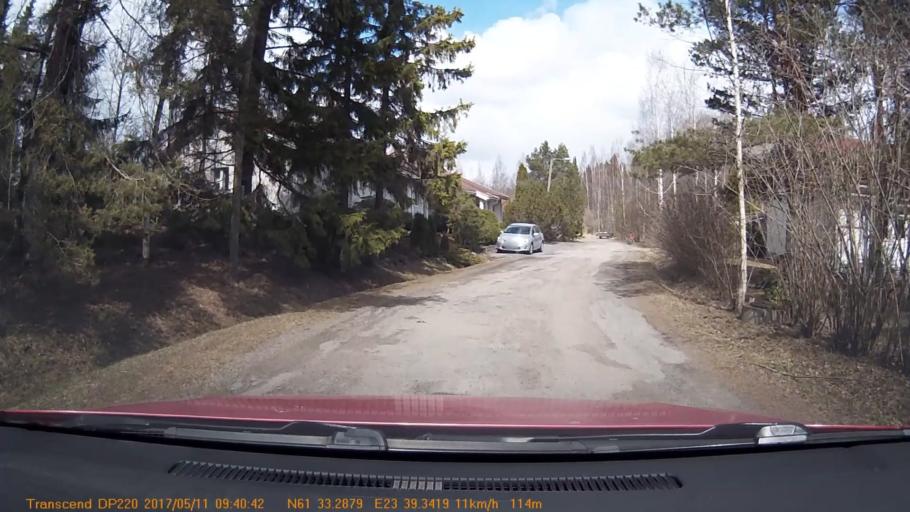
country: FI
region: Pirkanmaa
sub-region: Tampere
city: Yloejaervi
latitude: 61.5548
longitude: 23.6557
